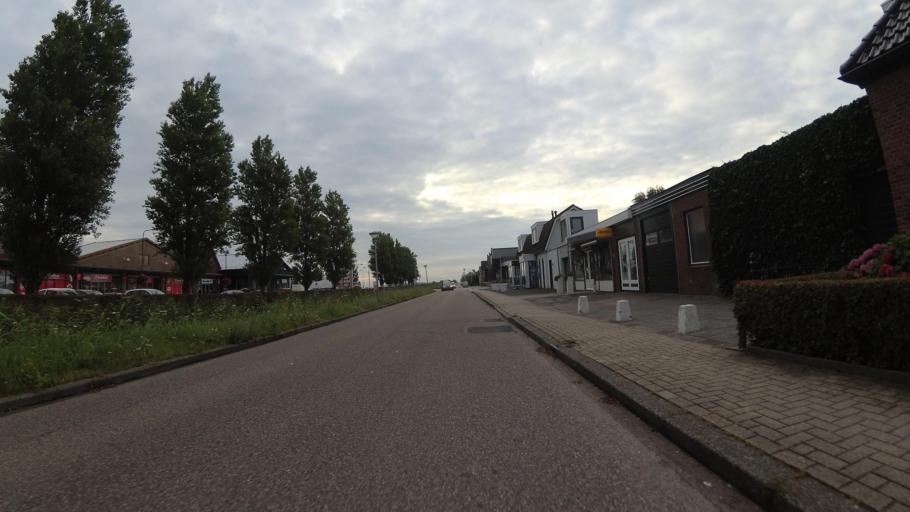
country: NL
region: North Holland
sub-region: Gemeente Den Helder
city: Den Helder
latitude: 52.8975
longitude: 4.7538
